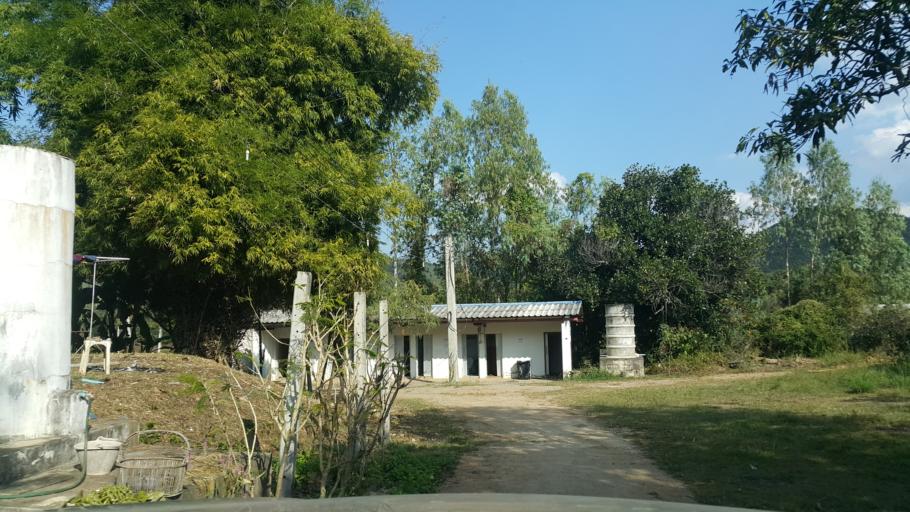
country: TH
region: Lamphun
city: Mae Tha
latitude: 18.5315
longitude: 99.1075
